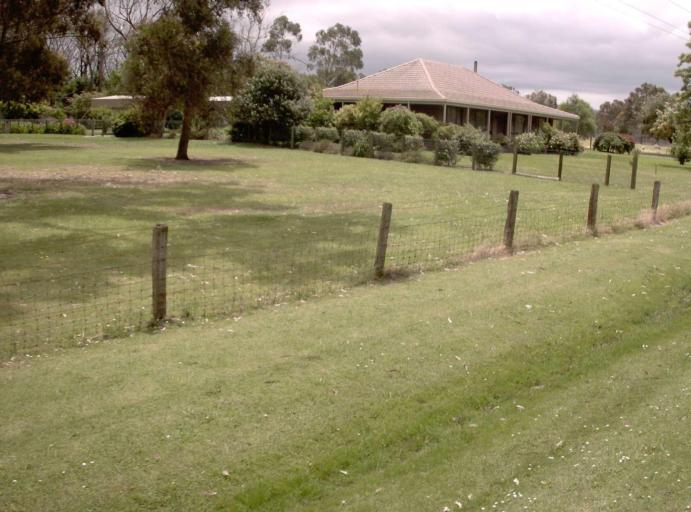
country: AU
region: Victoria
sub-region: Latrobe
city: Traralgon
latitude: -38.5401
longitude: 146.6568
